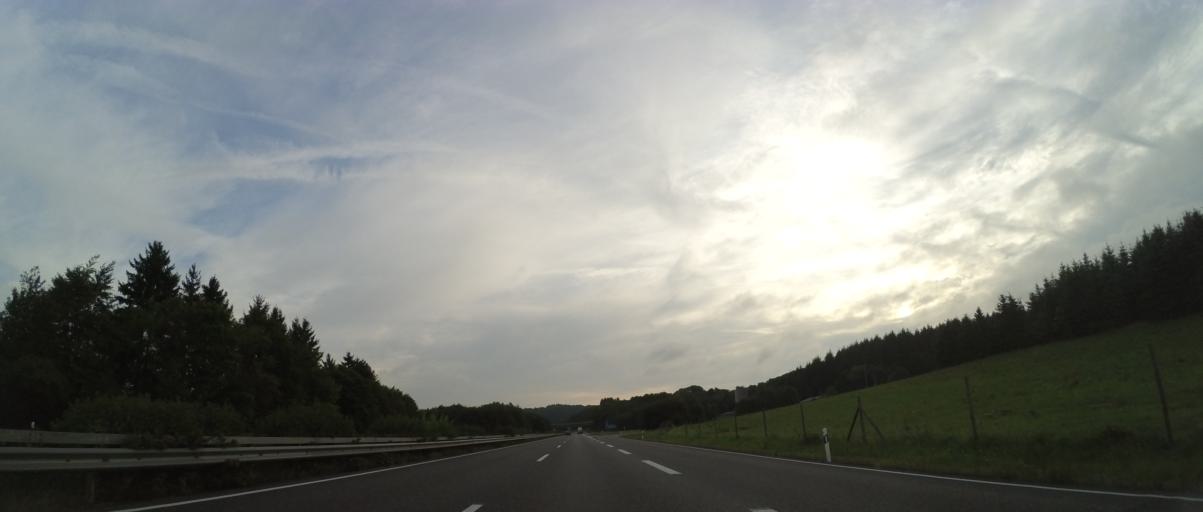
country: DE
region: Rheinland-Pfalz
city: Mehren
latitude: 50.1651
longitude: 6.8856
